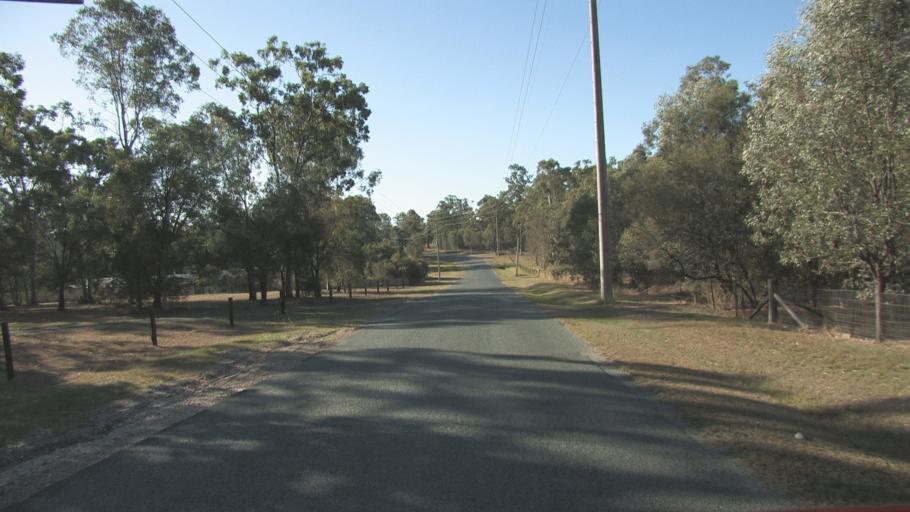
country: AU
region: Queensland
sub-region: Logan
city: North Maclean
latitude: -27.7956
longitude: 153.0422
